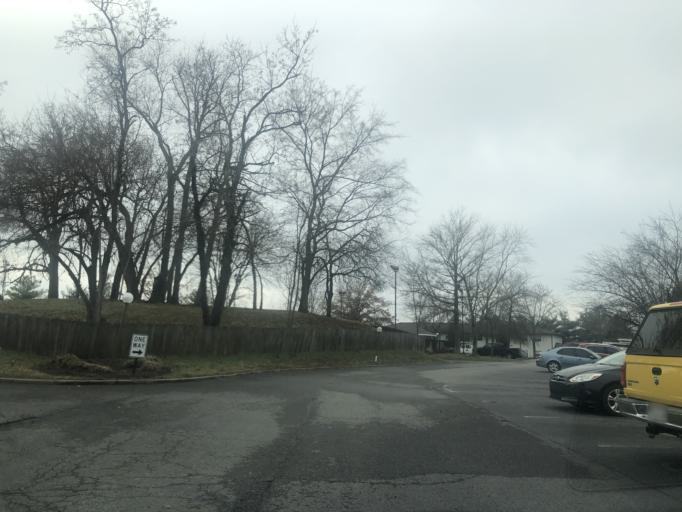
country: US
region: Tennessee
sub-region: Rutherford County
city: La Vergne
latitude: 36.0738
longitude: -86.6407
